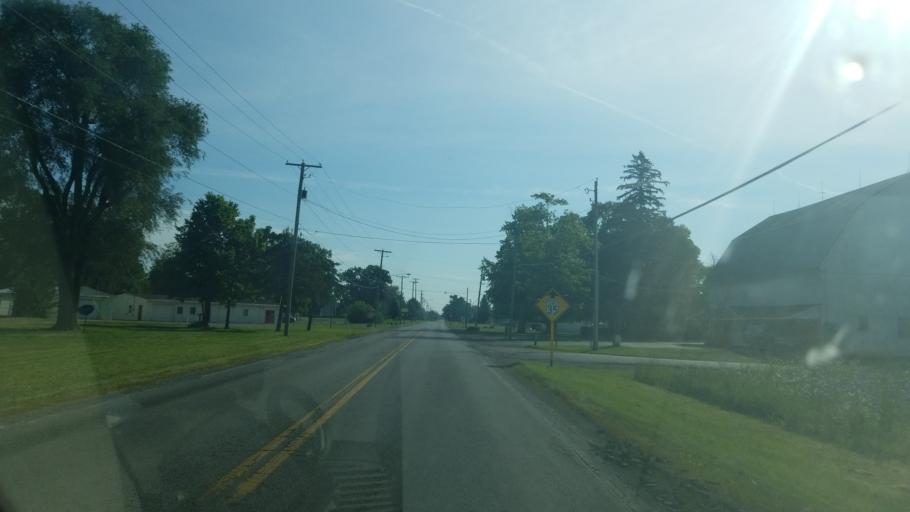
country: US
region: Ohio
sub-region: Hancock County
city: Findlay
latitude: 41.0142
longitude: -83.6815
